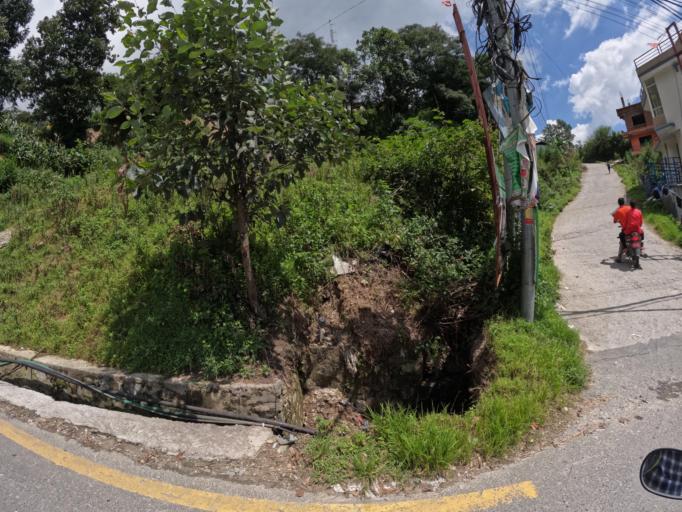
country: NP
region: Central Region
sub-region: Bagmati Zone
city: Kathmandu
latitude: 27.7893
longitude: 85.3303
